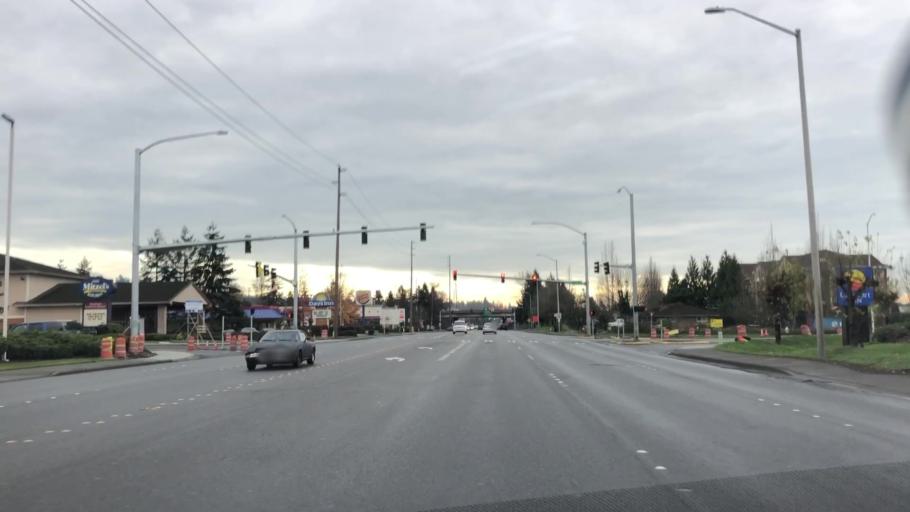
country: US
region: Washington
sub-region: King County
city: Kent
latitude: 47.4016
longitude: -122.2281
